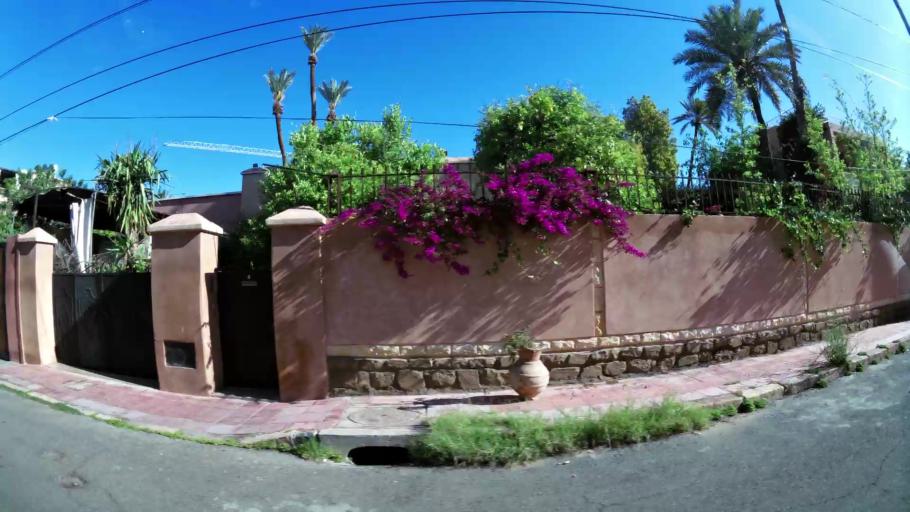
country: MA
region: Marrakech-Tensift-Al Haouz
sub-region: Marrakech
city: Marrakesh
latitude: 31.6434
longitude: -8.0168
